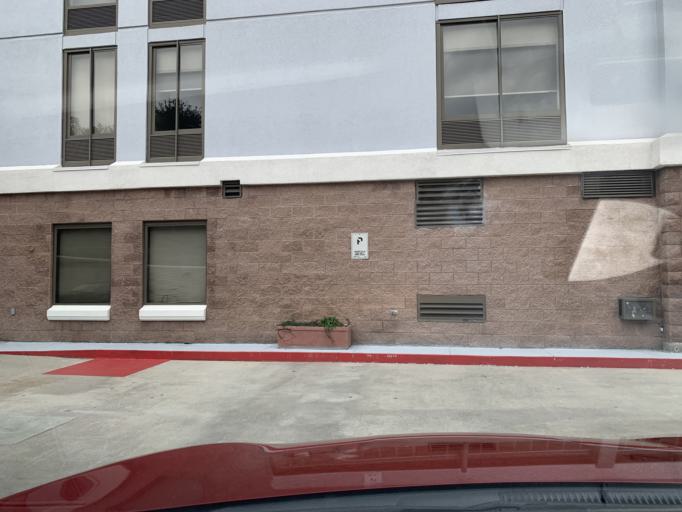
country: US
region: Georgia
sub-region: Fulton County
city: Sandy Springs
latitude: 33.9182
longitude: -84.3598
